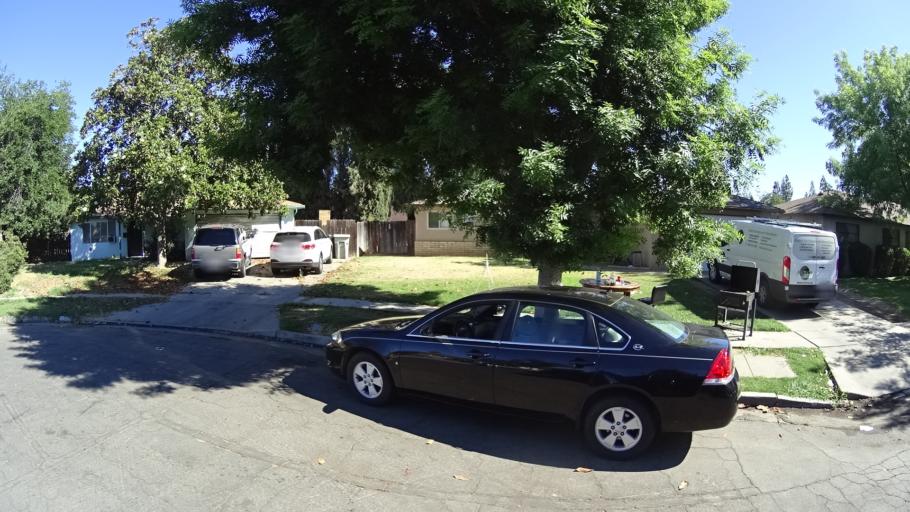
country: US
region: California
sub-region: Fresno County
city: West Park
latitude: 36.8058
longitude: -119.8497
